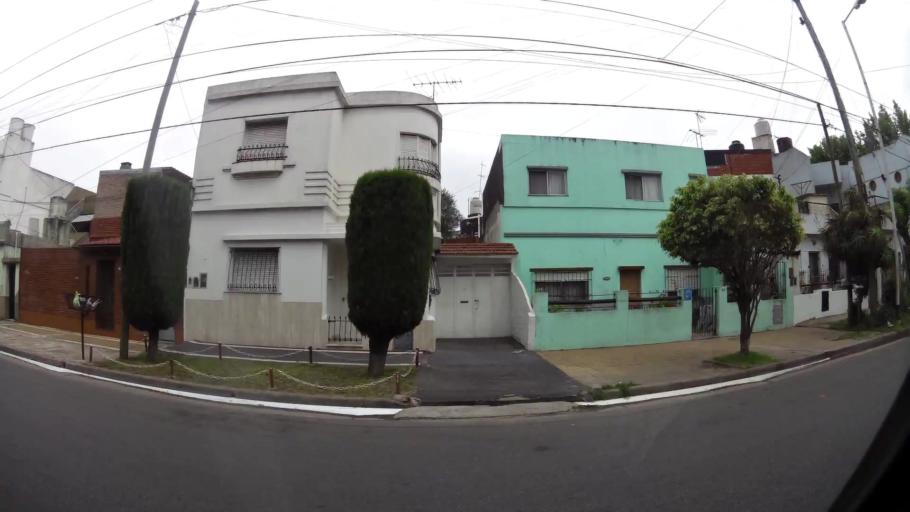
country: AR
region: Buenos Aires
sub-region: Partido de Avellaneda
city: Avellaneda
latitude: -34.6699
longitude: -58.3441
